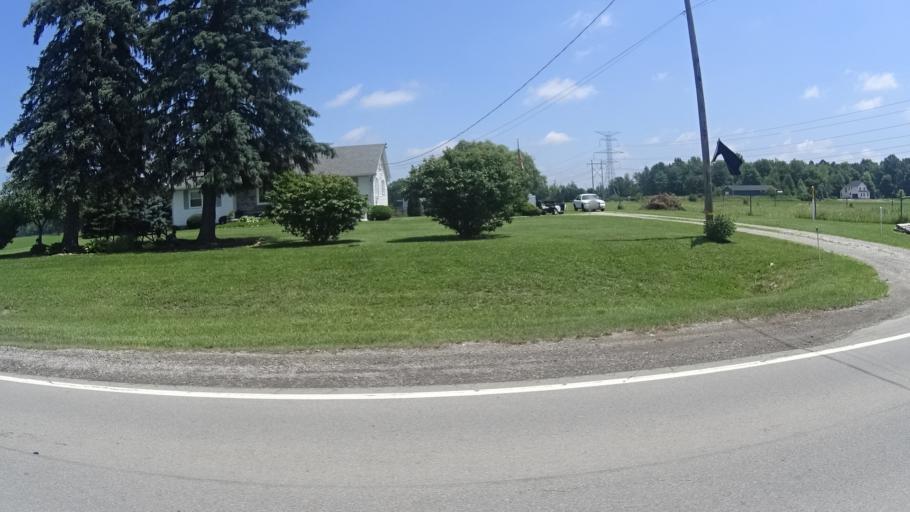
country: US
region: Ohio
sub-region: Lorain County
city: Vermilion
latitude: 41.3451
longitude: -82.3598
